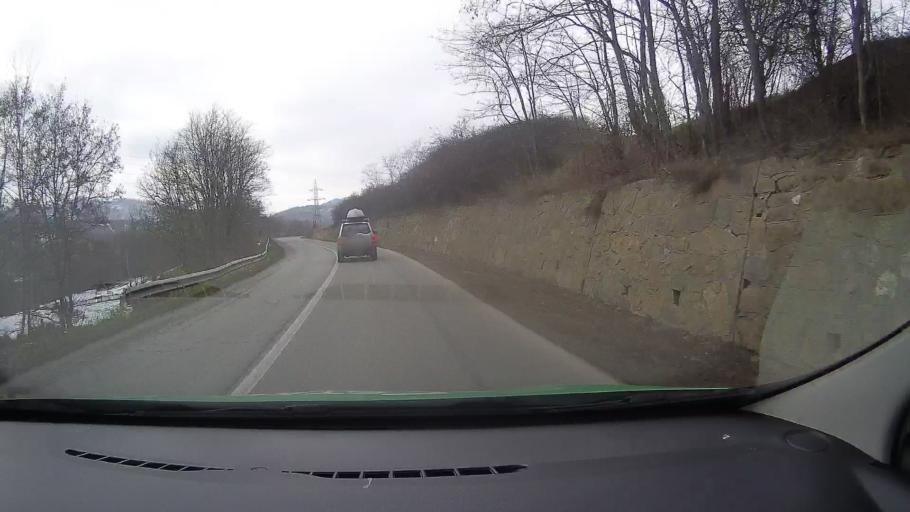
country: RO
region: Alba
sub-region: Oras Zlatna
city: Fenes
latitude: 46.0915
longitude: 23.2884
